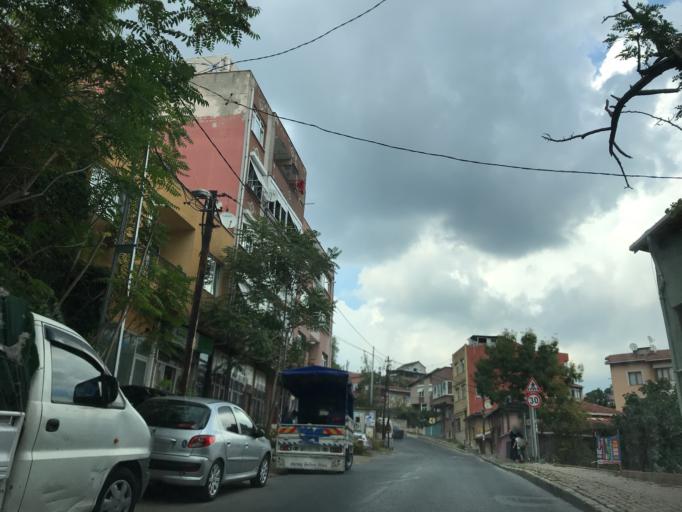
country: TR
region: Istanbul
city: Arikoey
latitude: 41.1749
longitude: 29.0522
